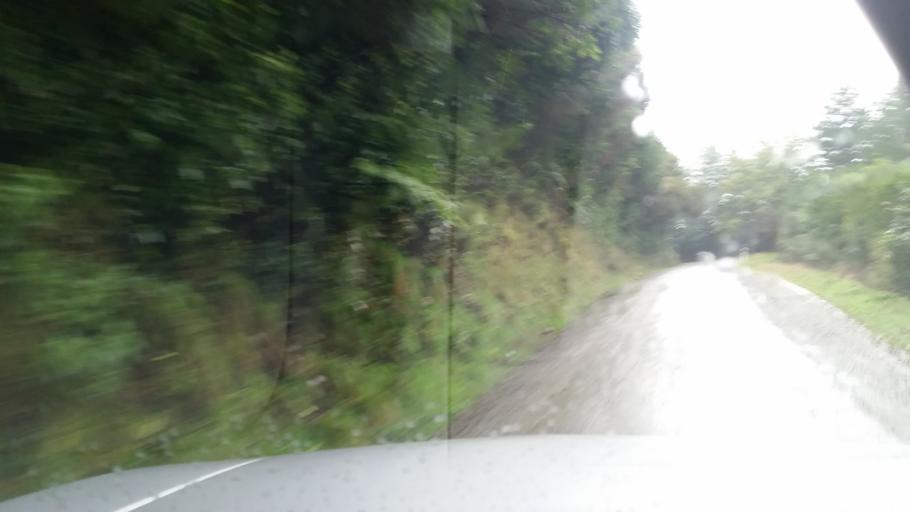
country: NZ
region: Marlborough
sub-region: Marlborough District
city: Picton
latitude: -41.1388
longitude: 174.0503
